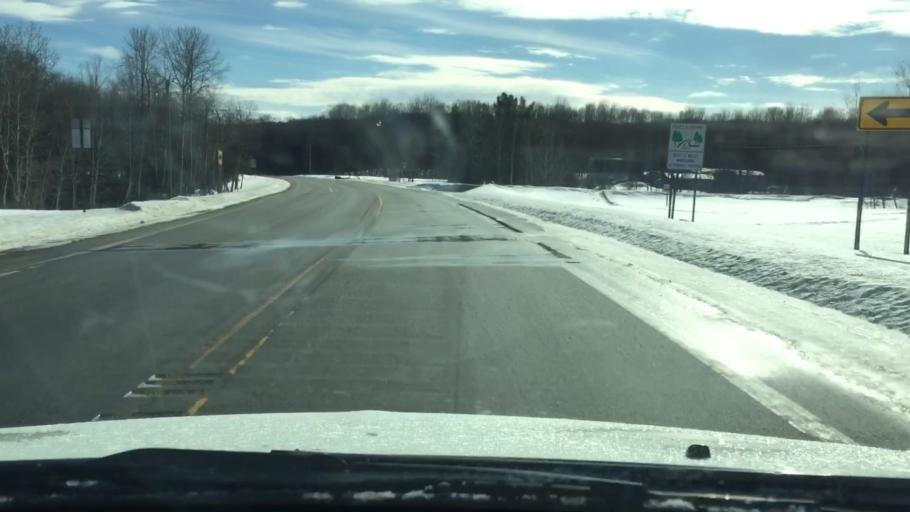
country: US
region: Michigan
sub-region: Antrim County
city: Mancelona
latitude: 44.9936
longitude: -85.0620
